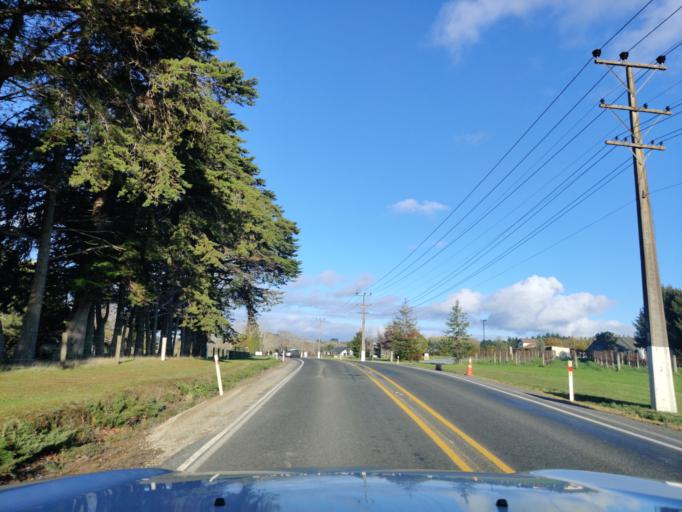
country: NZ
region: Auckland
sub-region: Auckland
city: Pakuranga
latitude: -36.9573
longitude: 174.9707
